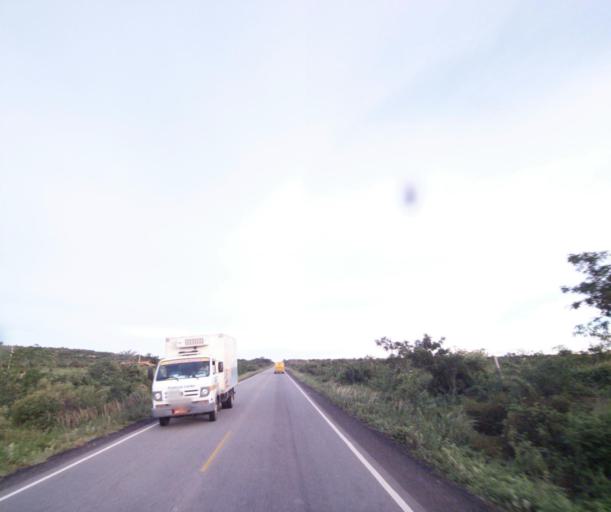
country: BR
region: Bahia
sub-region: Brumado
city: Brumado
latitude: -14.2402
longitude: -41.8806
